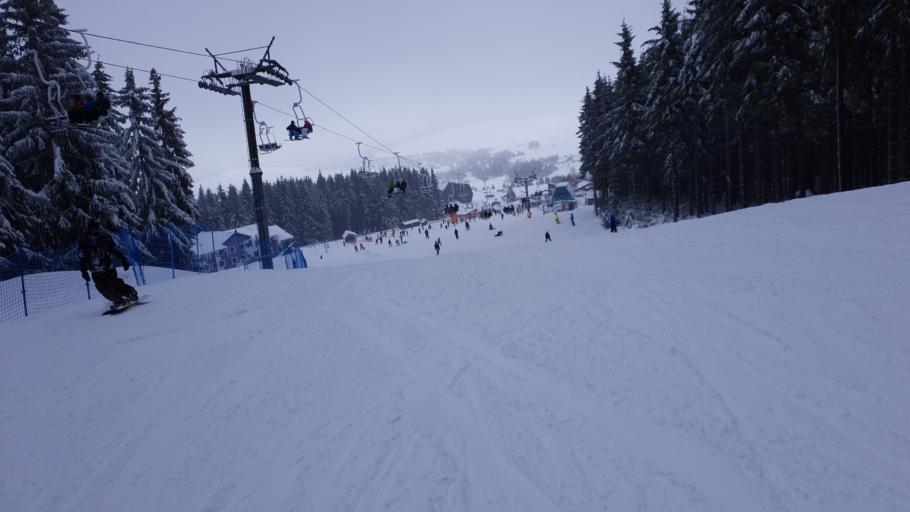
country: DE
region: Saxony
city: Kurort Oberwiesenthal
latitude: 50.4017
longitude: 12.9810
